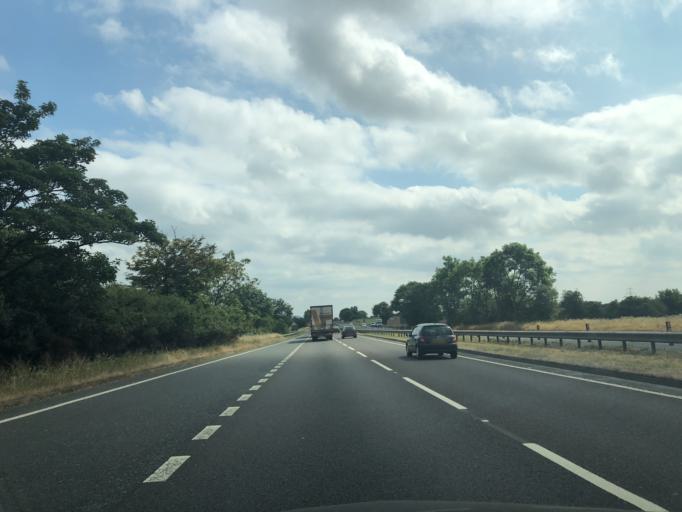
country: GB
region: England
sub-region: Stockton-on-Tees
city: Yarm
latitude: 54.4267
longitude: -1.3202
